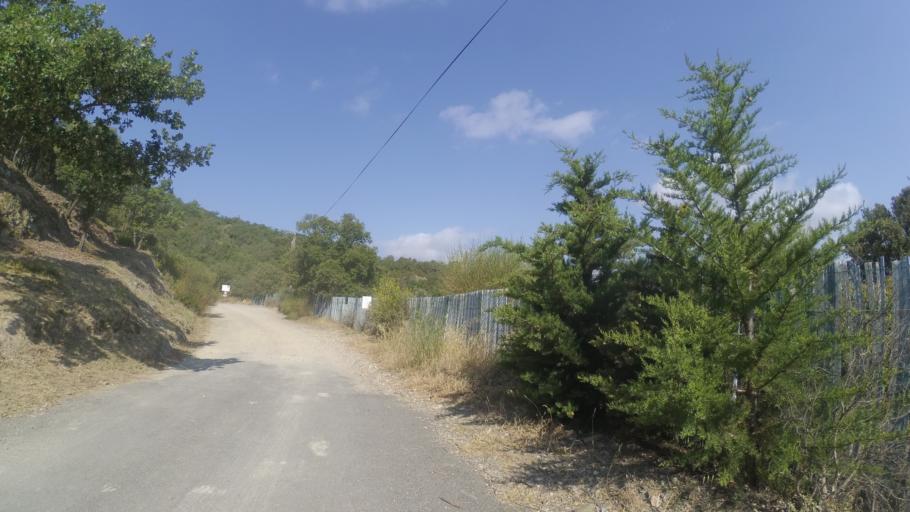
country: FR
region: Languedoc-Roussillon
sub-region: Departement des Pyrenees-Orientales
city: Millas
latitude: 42.6291
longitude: 2.6814
